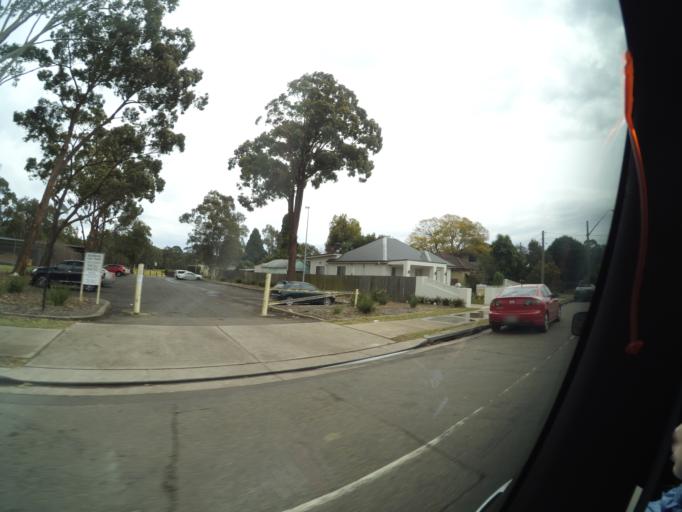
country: AU
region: New South Wales
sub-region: Auburn
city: Berala
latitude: -33.8649
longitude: 151.0183
